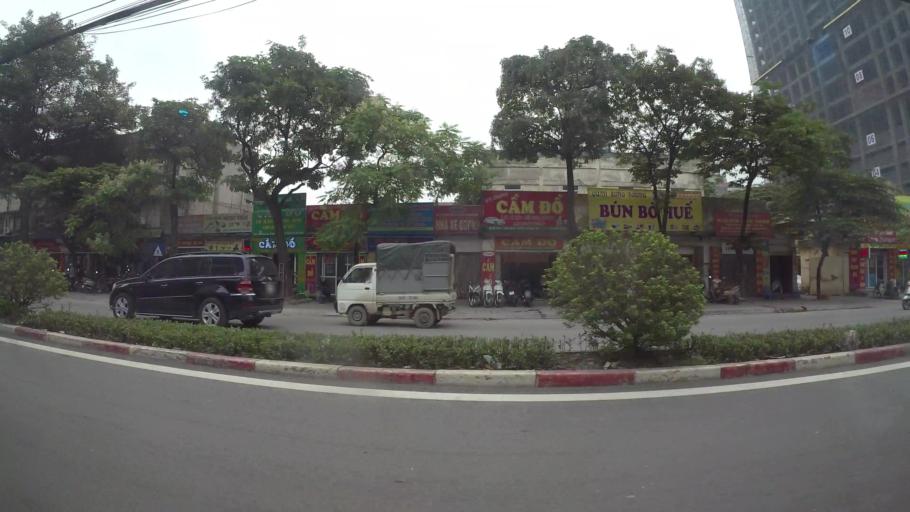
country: VN
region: Ha Noi
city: Ha Dong
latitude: 20.9745
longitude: 105.7778
